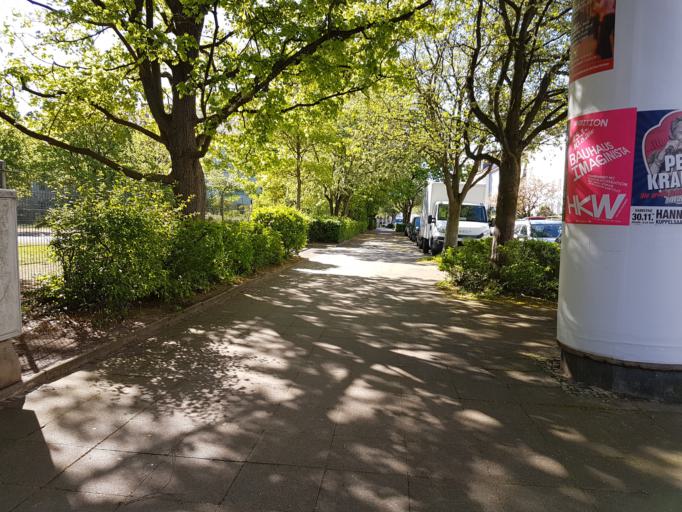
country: DE
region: Lower Saxony
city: Hannover
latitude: 52.3627
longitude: 9.7458
